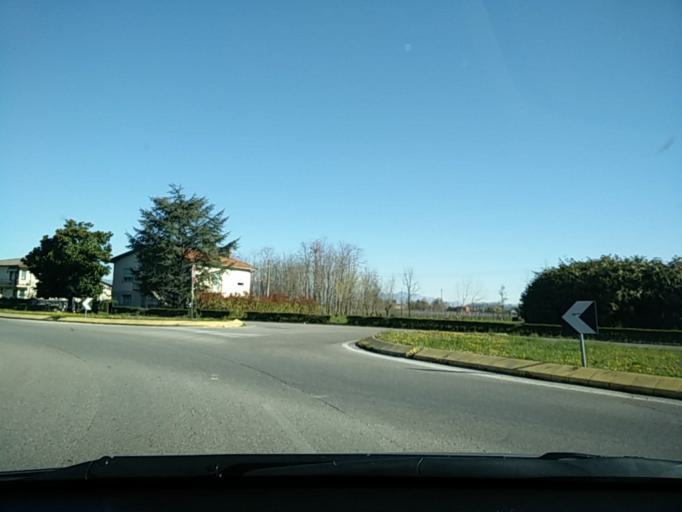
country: IT
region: Veneto
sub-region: Provincia di Treviso
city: Piavon
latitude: 45.7705
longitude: 12.5157
